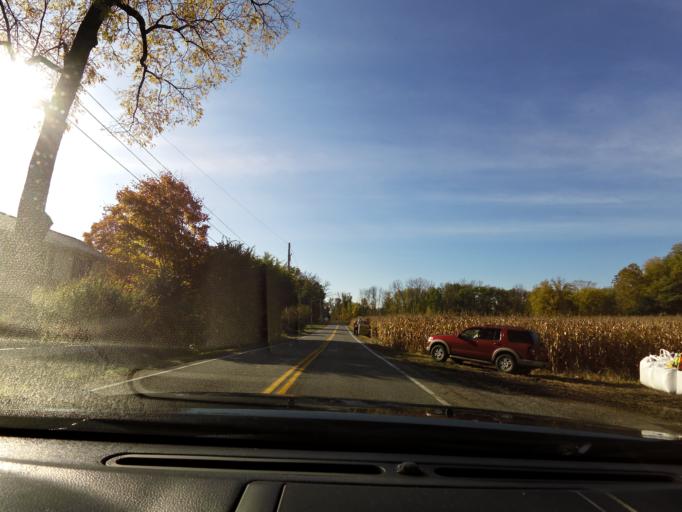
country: US
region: New York
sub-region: Livingston County
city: Mount Morris
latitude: 42.7675
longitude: -77.8741
